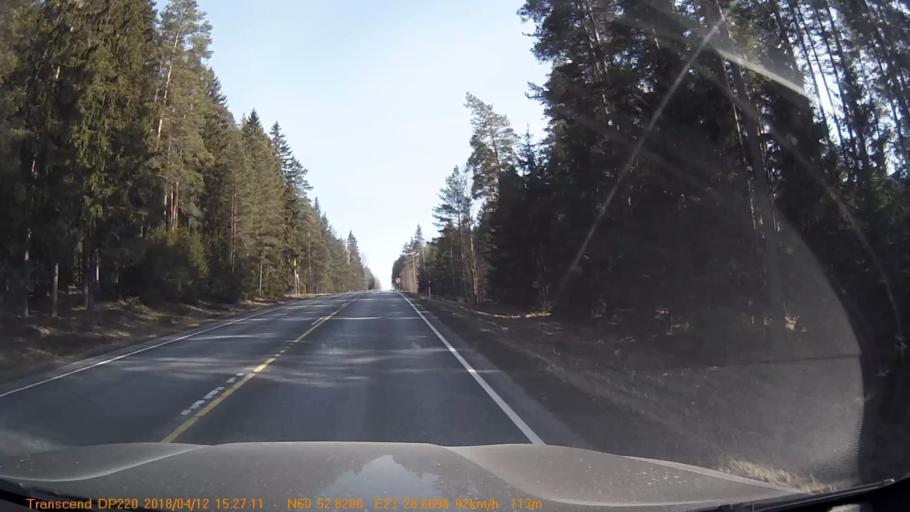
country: FI
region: Haeme
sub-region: Forssa
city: Jokioinen
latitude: 60.8796
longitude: 23.4796
